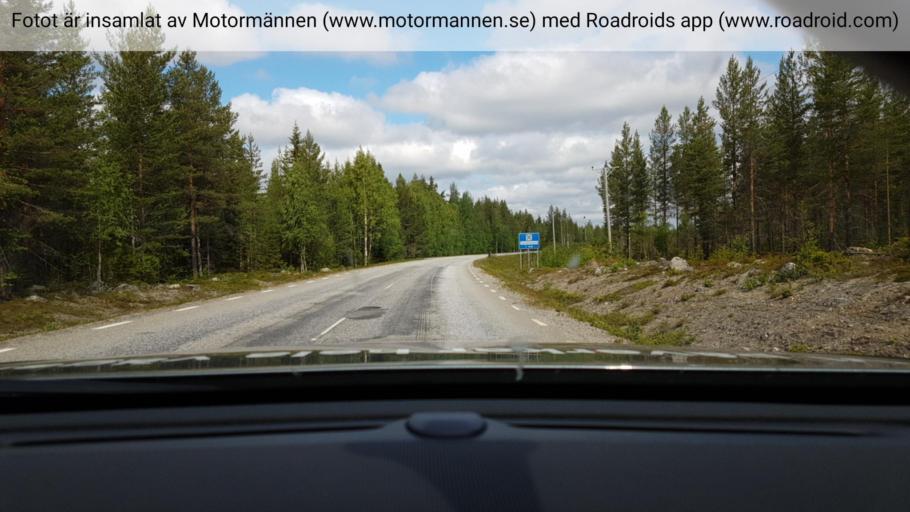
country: SE
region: Vaesterbotten
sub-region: Lycksele Kommun
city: Lycksele
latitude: 64.8603
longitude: 18.7249
